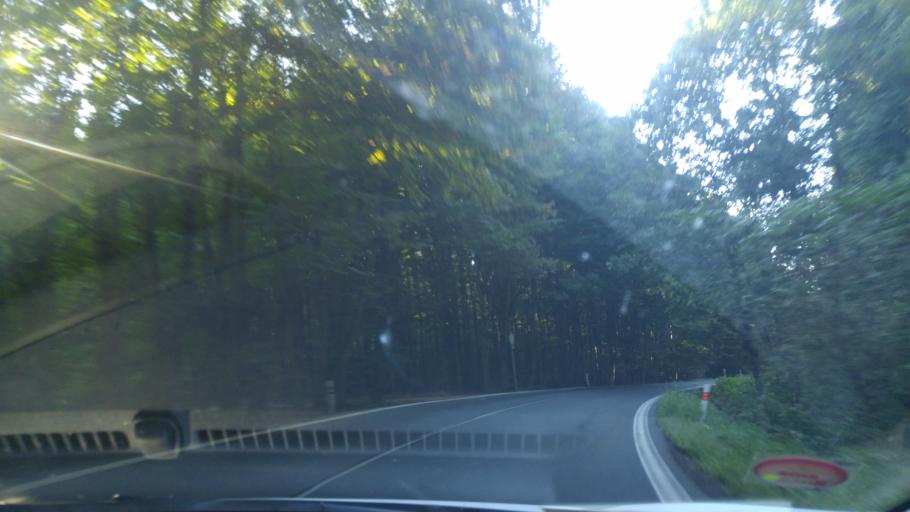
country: CZ
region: South Moravian
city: Veverska Bityska
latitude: 49.2563
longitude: 16.4737
